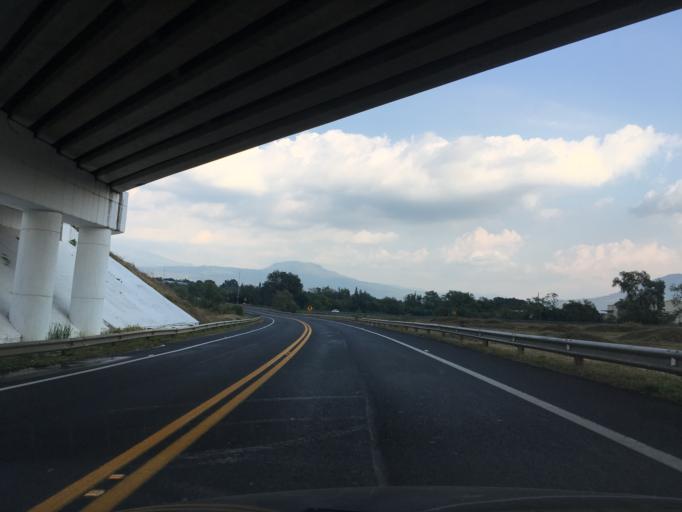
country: MX
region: Michoacan
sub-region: Ziracuaretiro
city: Patuan
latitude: 19.4159
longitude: -101.9366
